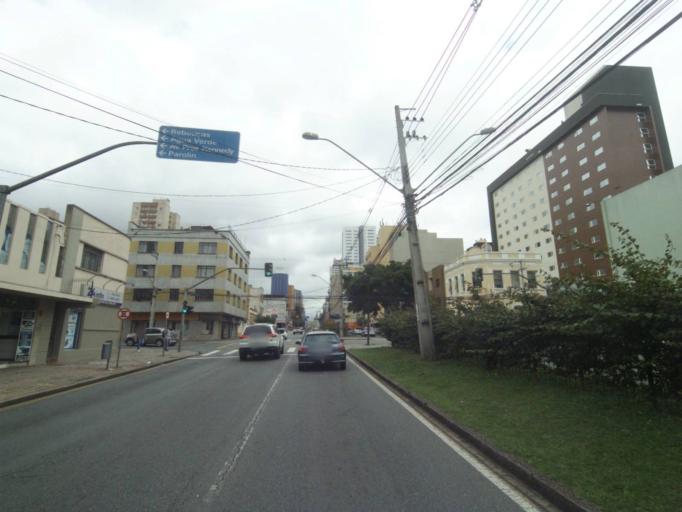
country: BR
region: Parana
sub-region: Curitiba
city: Curitiba
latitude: -25.4387
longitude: -49.2733
